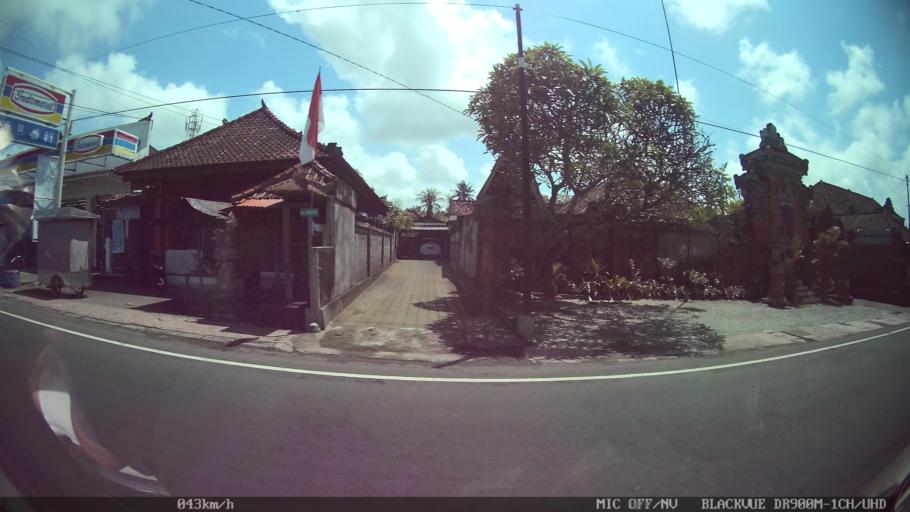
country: ID
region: Bali
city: Banjar Pasekan
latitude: -8.6030
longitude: 115.2783
